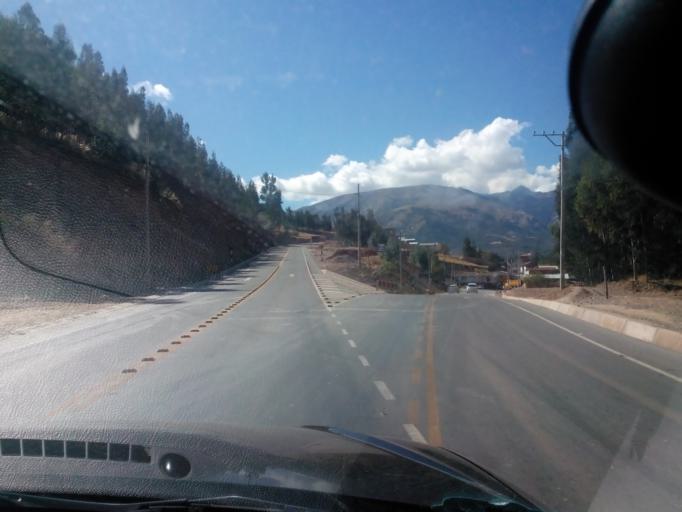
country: PE
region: Cusco
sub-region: Provincia de Quispicanchis
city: Huaro
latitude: -13.6854
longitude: -71.6303
